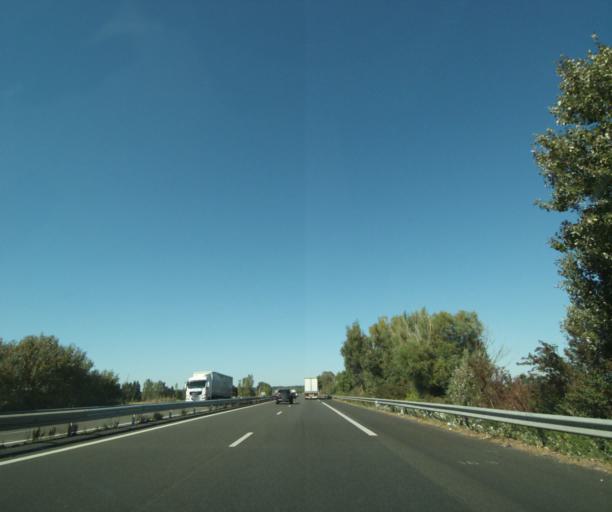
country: FR
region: Languedoc-Roussillon
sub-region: Departement du Gard
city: Bellegarde
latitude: 43.7177
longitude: 4.5105
